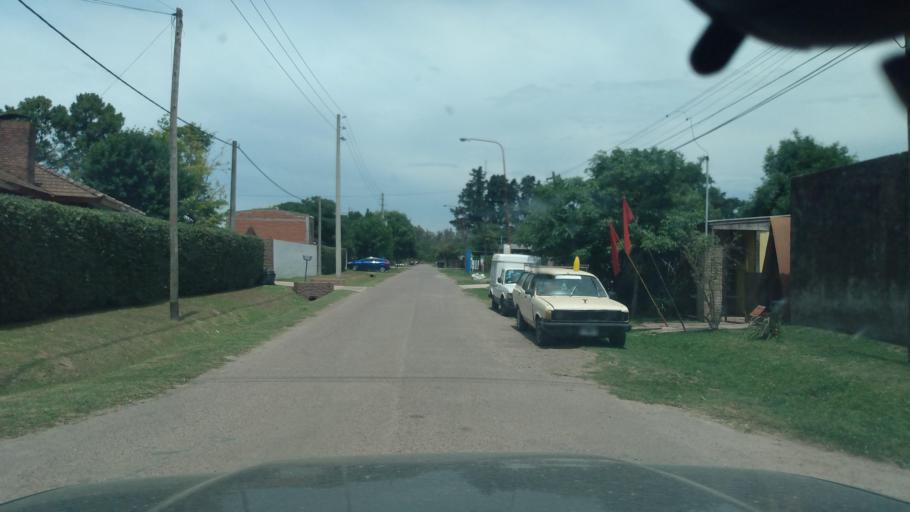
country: AR
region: Buenos Aires
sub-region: Partido de Lujan
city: Lujan
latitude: -34.5451
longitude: -59.1417
